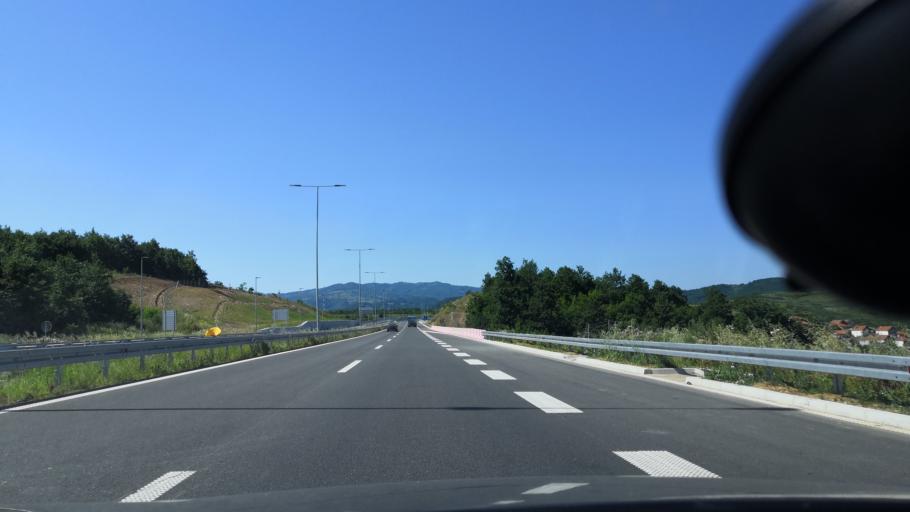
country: RS
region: Central Serbia
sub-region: Pcinjski Okrug
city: Vladicin Han
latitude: 42.7046
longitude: 22.0741
